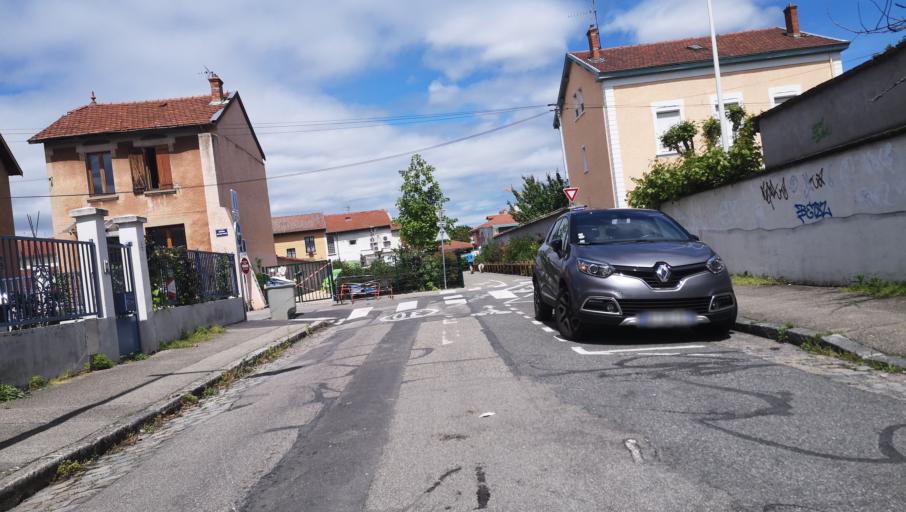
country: FR
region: Rhone-Alpes
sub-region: Departement du Rhone
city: Villeurbanne
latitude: 45.7519
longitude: 4.8745
